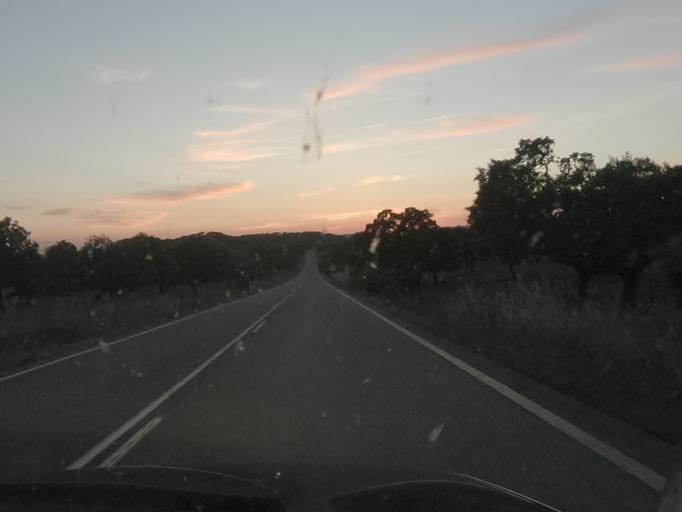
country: ES
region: Extremadura
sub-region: Provincia de Caceres
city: Piedras Albas
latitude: 39.7867
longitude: -6.9487
